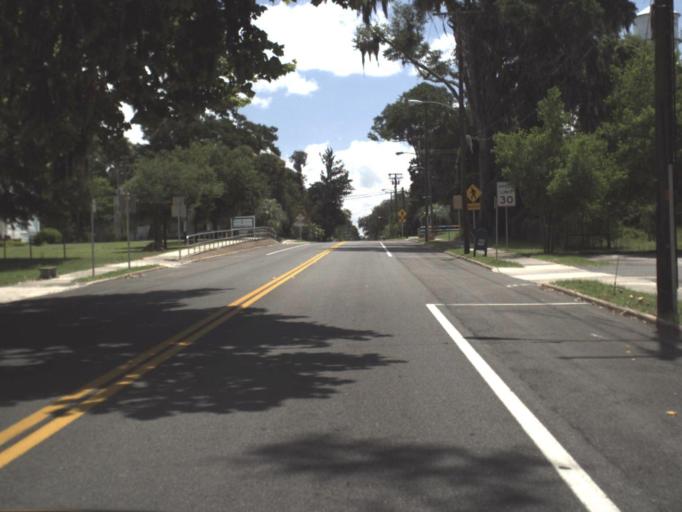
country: US
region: Florida
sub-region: Suwannee County
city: Wellborn
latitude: 30.3298
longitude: -82.7581
